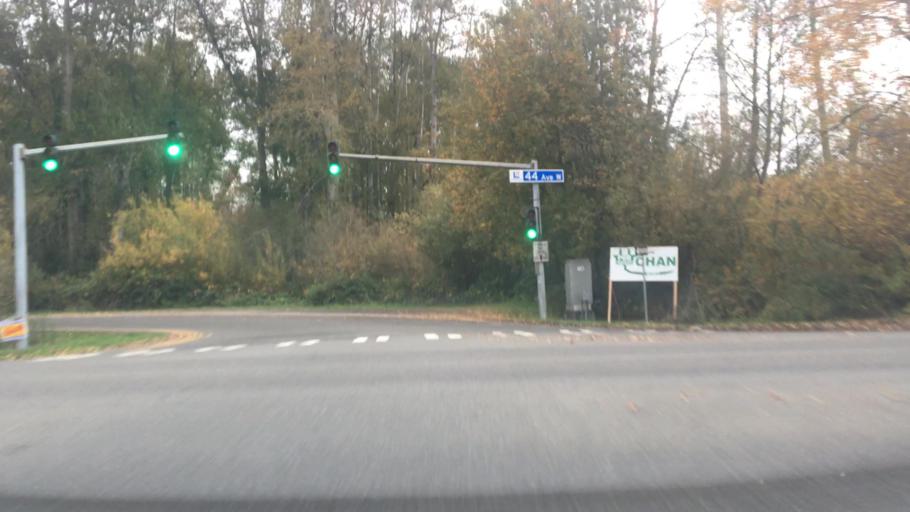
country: US
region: Washington
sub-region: Snohomish County
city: Alderwood Manor
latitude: 47.8124
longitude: -122.2924
